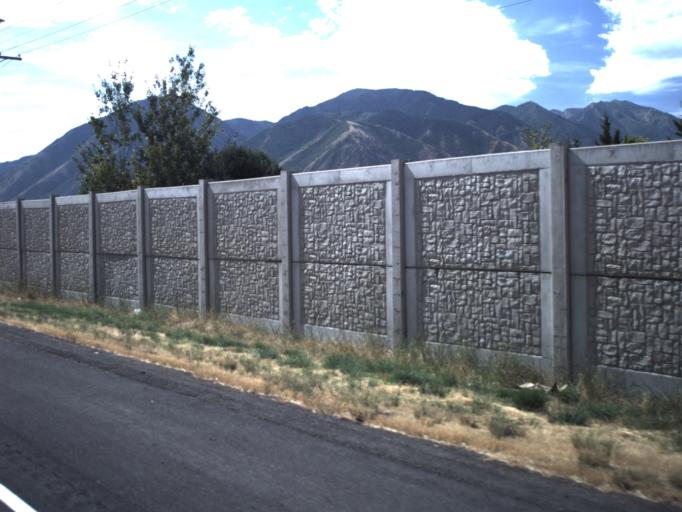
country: US
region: Utah
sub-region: Utah County
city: Spanish Fork
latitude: 40.1073
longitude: -111.6276
